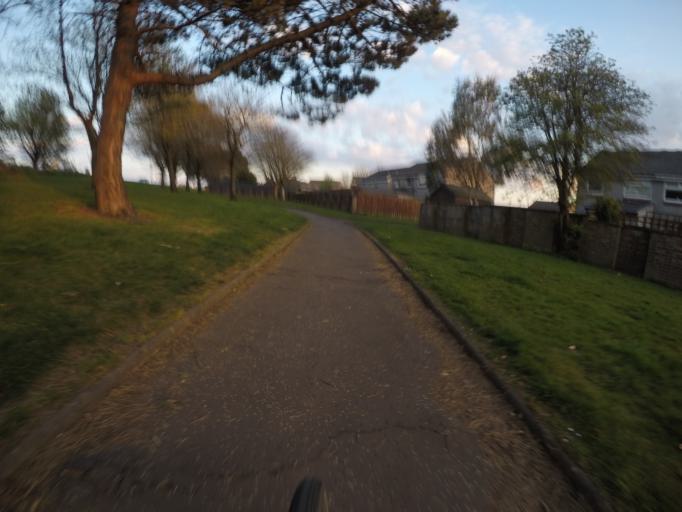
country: GB
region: Scotland
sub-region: South Ayrshire
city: Troon
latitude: 55.5657
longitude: -4.6387
